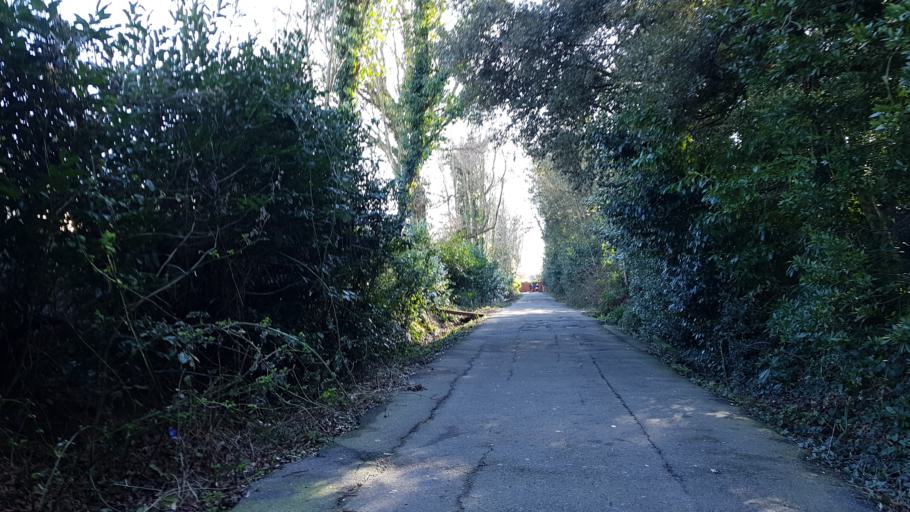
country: GB
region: England
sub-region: Isle of Wight
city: Ryde
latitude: 50.7249
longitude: -1.1448
